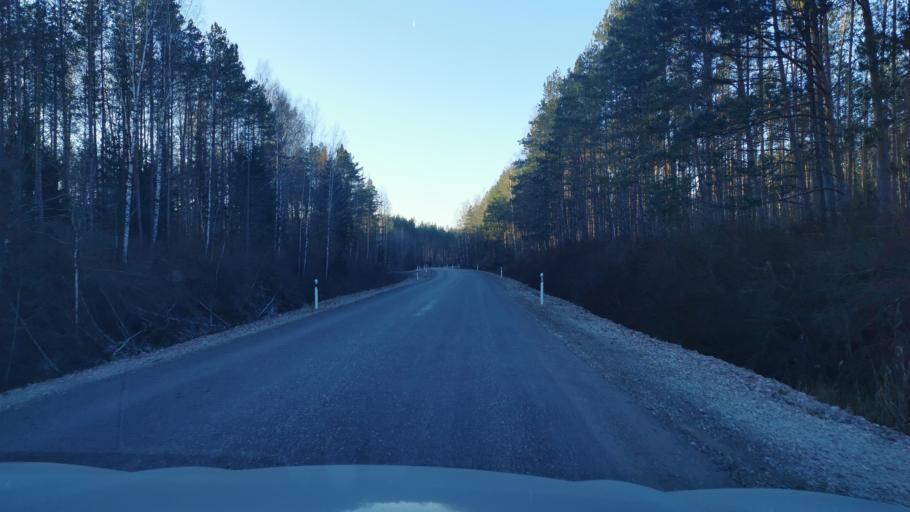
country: EE
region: Ida-Virumaa
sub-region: Kohtla-Nomme vald
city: Kohtla-Nomme
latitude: 59.3407
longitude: 27.1374
